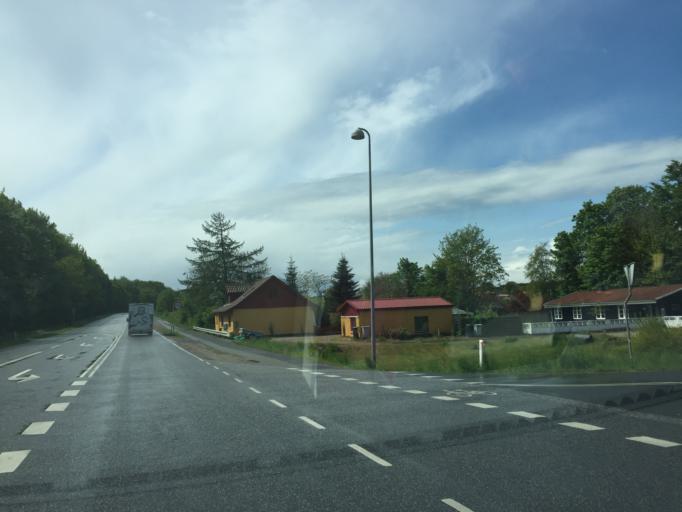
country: DK
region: Zealand
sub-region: Soro Kommune
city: Soro
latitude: 55.4440
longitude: 11.5358
